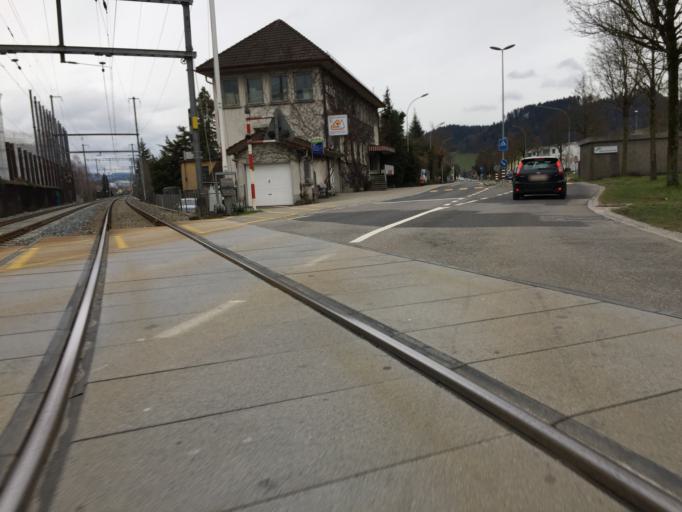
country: CH
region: Bern
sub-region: Emmental District
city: Oberburg
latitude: 47.0484
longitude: 7.6224
